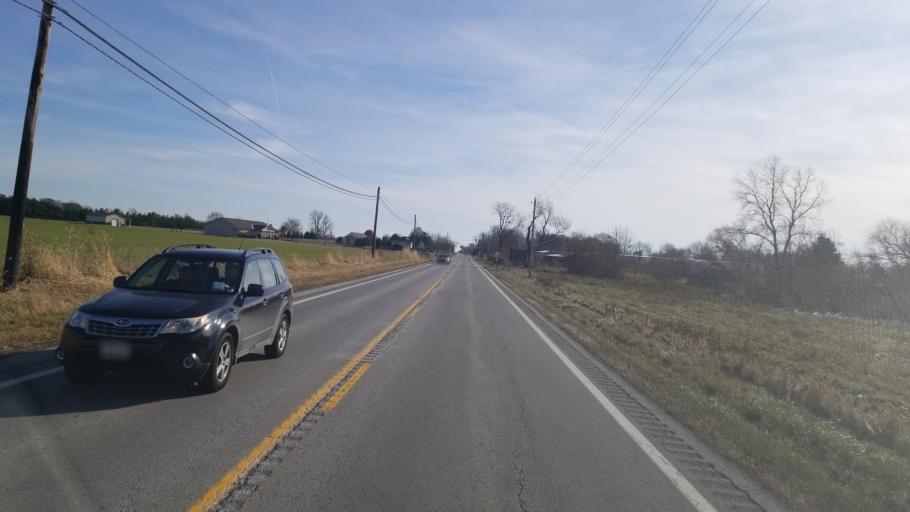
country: US
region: Ohio
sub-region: Huron County
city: Norwalk
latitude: 41.2110
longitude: -82.5891
